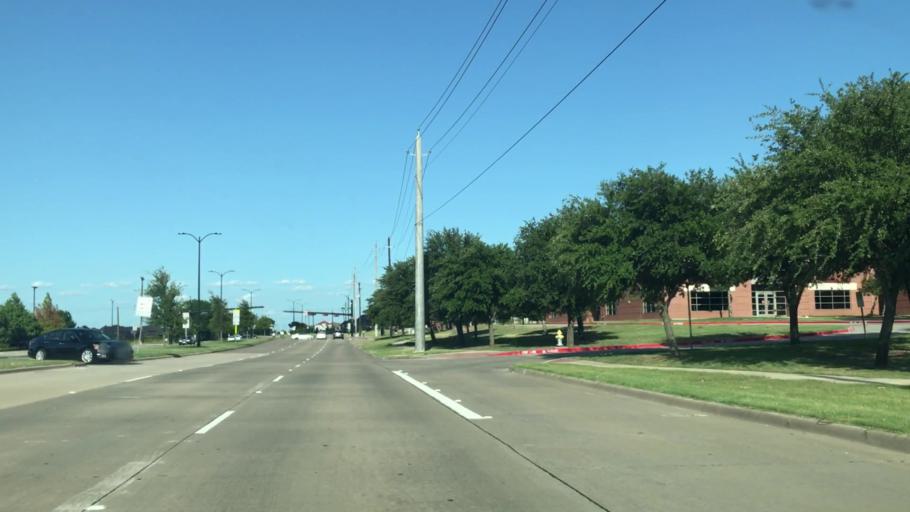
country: US
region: Texas
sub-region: Collin County
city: Frisco
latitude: 33.1374
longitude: -96.7700
